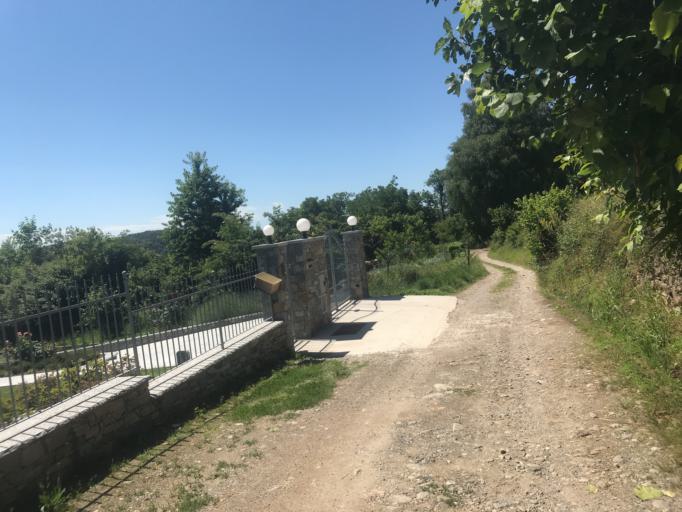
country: IT
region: Piedmont
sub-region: Provincia di Novara
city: Pisano
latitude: 45.7991
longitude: 8.5129
